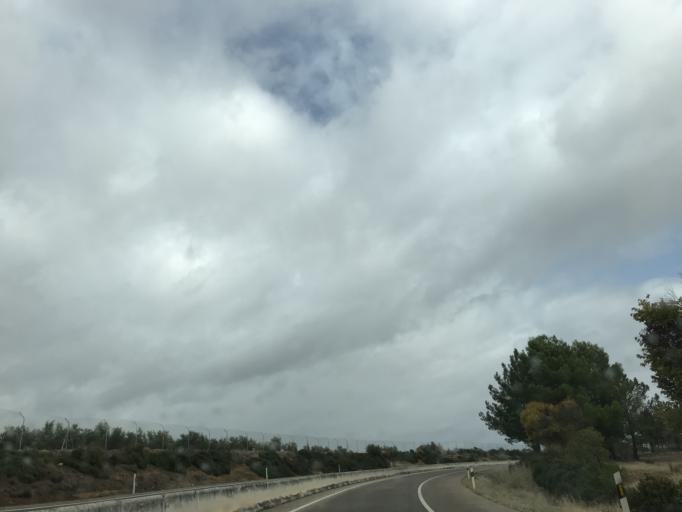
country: ES
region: Andalusia
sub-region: Provincia de Jaen
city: Bailen
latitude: 38.1236
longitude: -3.7615
